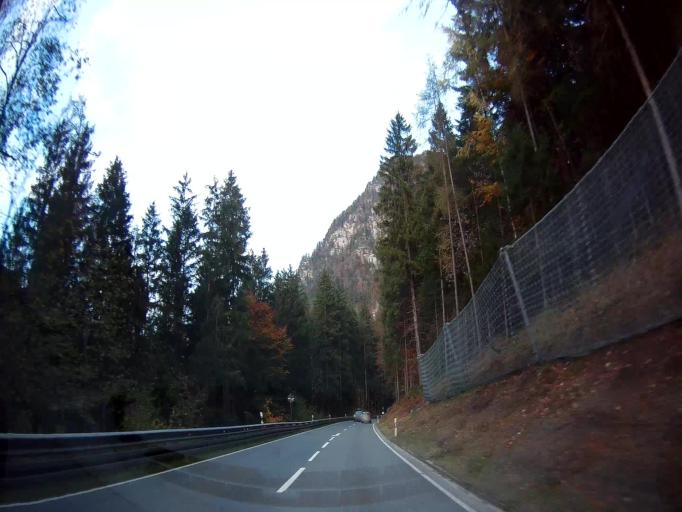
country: DE
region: Bavaria
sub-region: Upper Bavaria
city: Schneizlreuth
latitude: 47.6892
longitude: 12.8464
